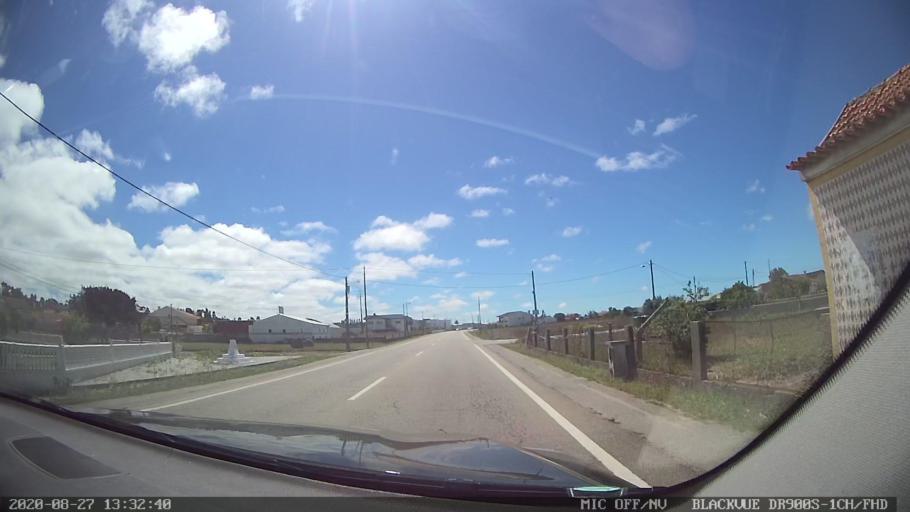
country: PT
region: Aveiro
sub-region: Vagos
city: Vagos
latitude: 40.4858
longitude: -8.6884
